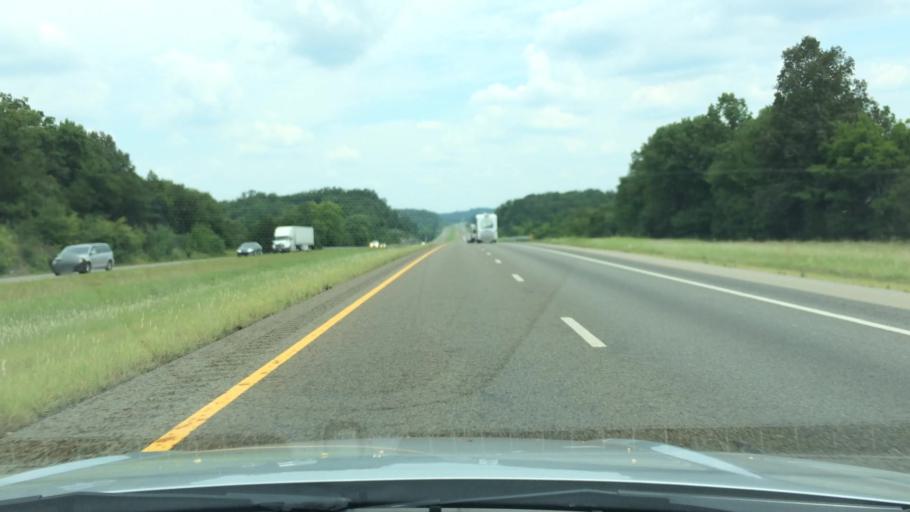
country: US
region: Tennessee
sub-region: Maury County
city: Columbia
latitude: 35.5927
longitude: -86.9023
